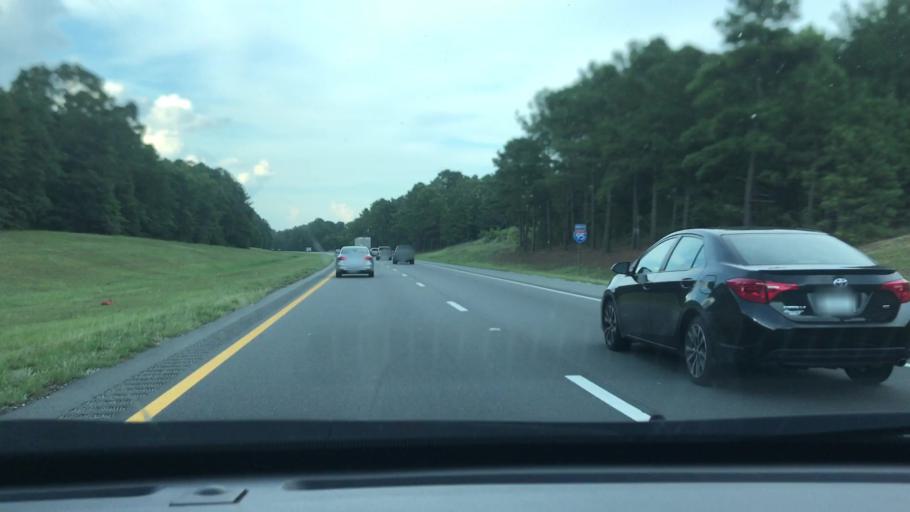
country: US
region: North Carolina
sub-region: Cumberland County
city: Hope Mills
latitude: 34.9415
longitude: -78.9143
